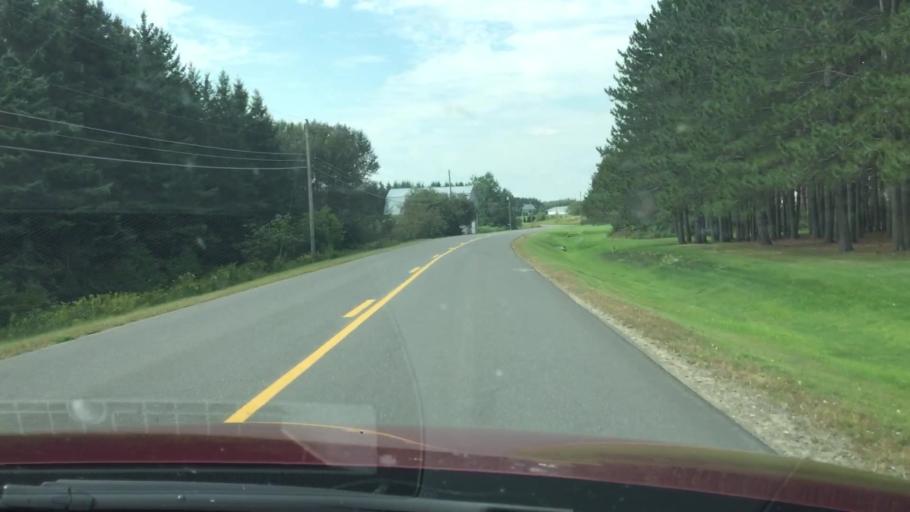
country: US
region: Maine
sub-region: Aroostook County
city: Caribou
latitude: 46.8297
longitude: -68.0159
